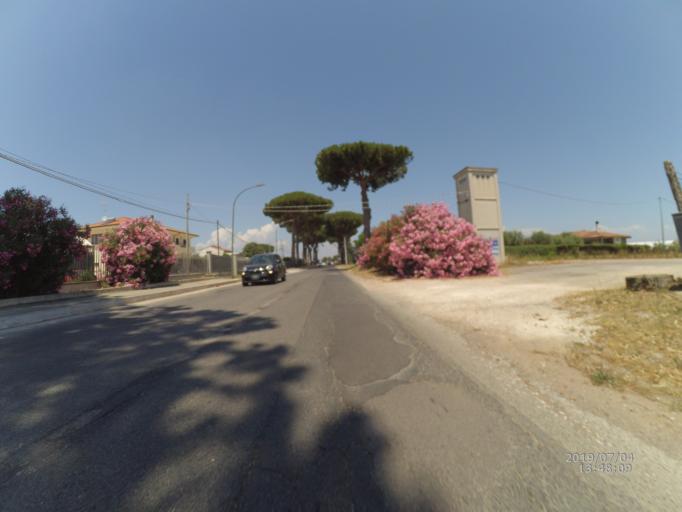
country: IT
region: Latium
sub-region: Provincia di Latina
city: San Felice Circeo
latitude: 41.2832
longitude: 13.1045
